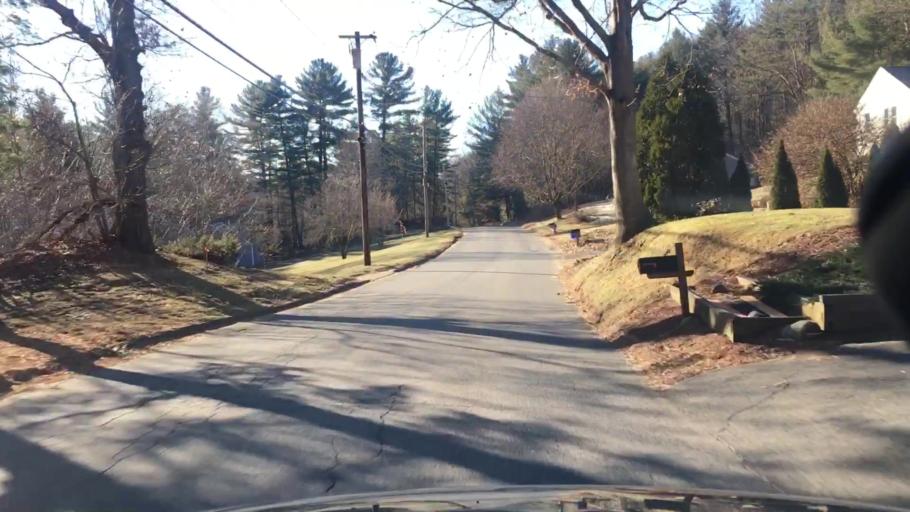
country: US
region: Connecticut
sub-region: Tolland County
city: Stafford
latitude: 41.9741
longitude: -72.2972
